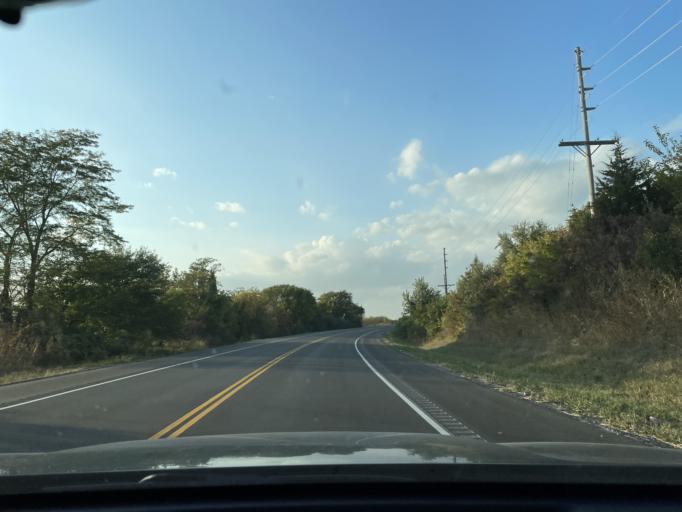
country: US
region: Missouri
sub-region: Andrew County
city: Country Club Village
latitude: 39.8415
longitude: -94.8679
